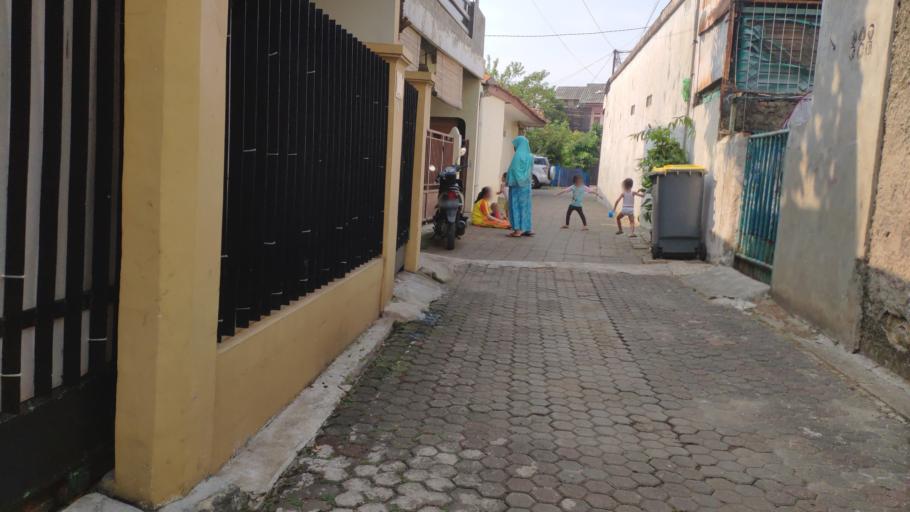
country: ID
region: West Java
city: Depok
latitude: -6.3235
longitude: 106.8127
